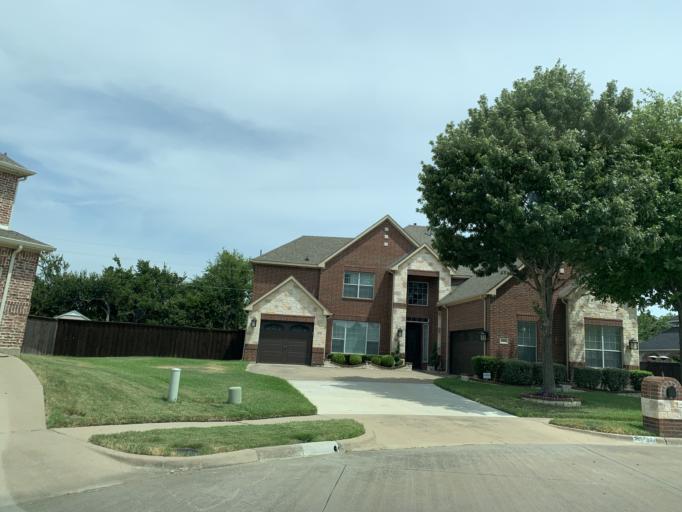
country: US
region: Texas
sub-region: Dallas County
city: Cedar Hill
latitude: 32.6515
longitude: -97.0026
